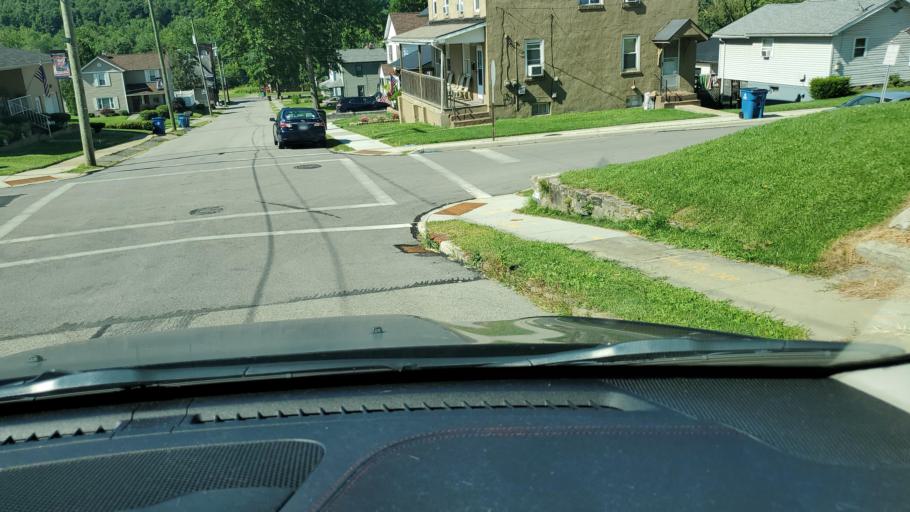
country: US
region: Ohio
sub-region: Mahoning County
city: Lowellville
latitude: 41.0415
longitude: -80.5388
